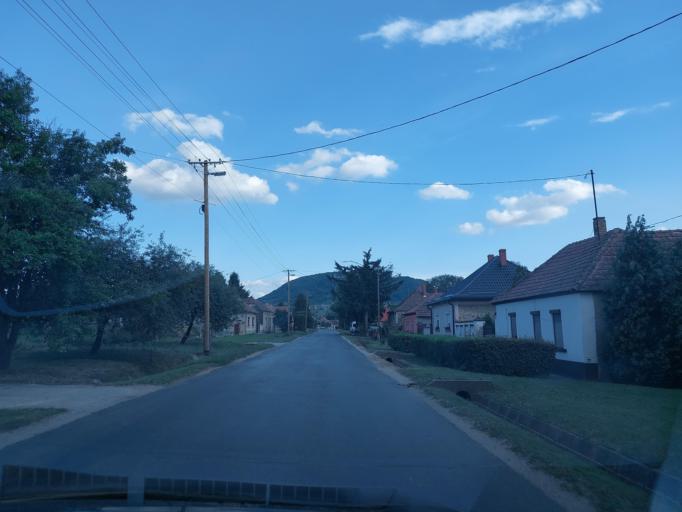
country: HU
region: Veszprem
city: Devecser
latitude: 47.1679
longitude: 17.3611
